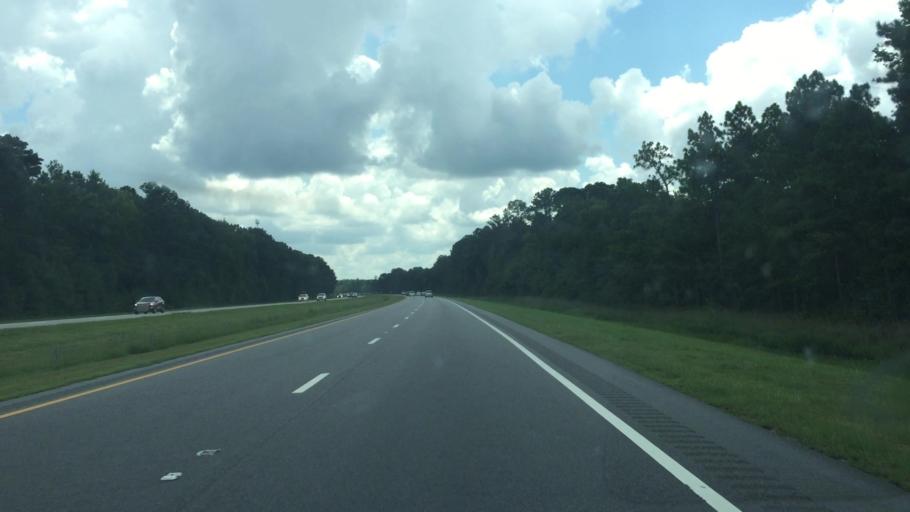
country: US
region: North Carolina
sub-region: Columbus County
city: Chadbourn
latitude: 34.4196
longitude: -78.9395
